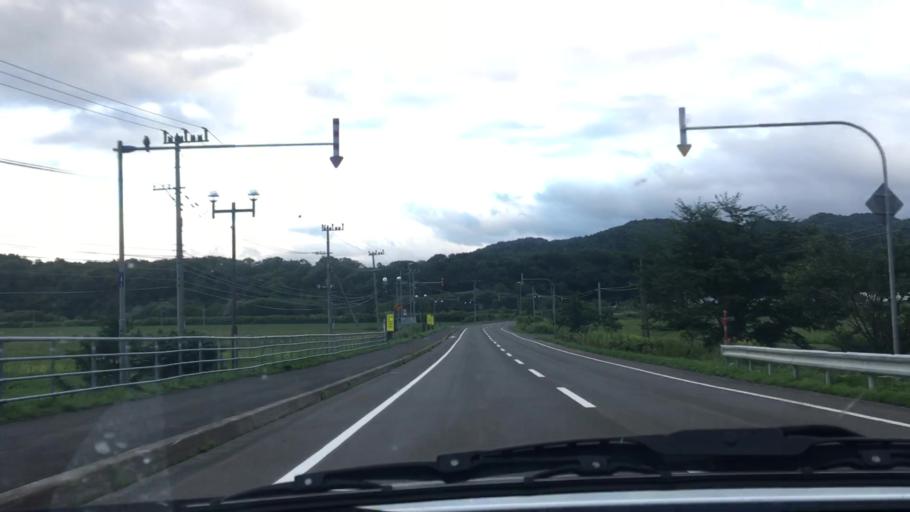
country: JP
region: Hokkaido
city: Shimo-furano
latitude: 42.9862
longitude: 142.3989
